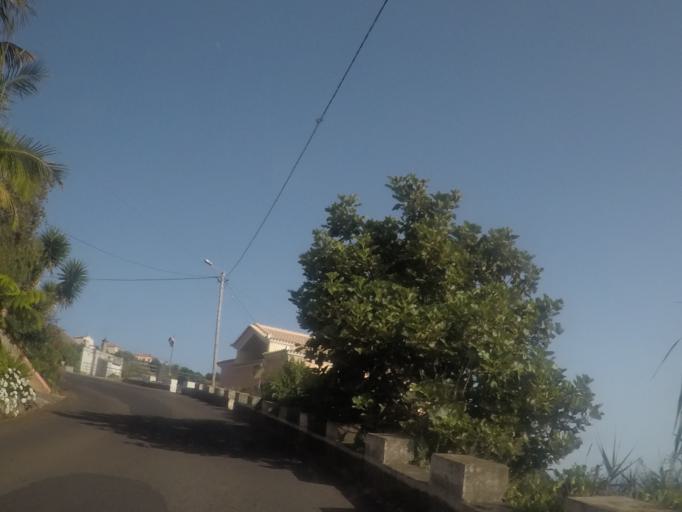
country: PT
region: Madeira
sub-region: Calheta
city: Arco da Calheta
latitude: 32.7063
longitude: -17.1292
